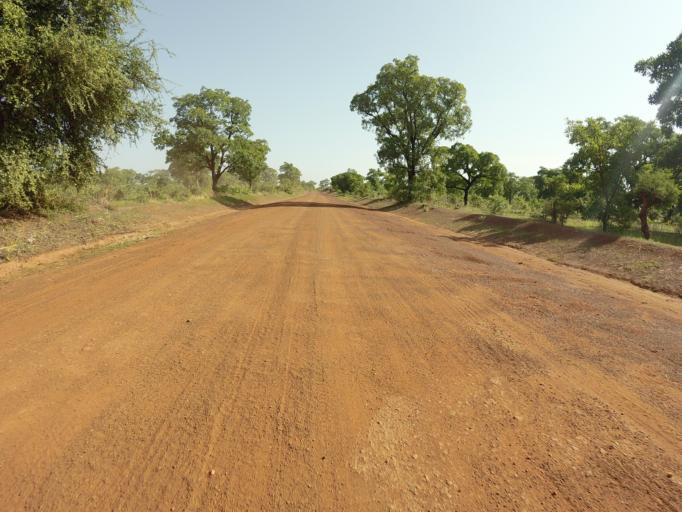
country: GH
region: Upper East
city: Bawku
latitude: 10.7383
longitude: -0.2011
